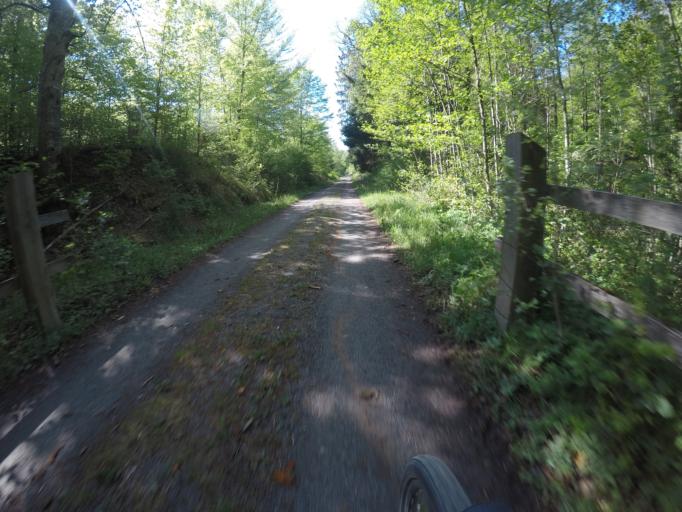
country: DE
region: Baden-Wuerttemberg
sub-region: Tuebingen Region
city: Dettenhausen
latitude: 48.5782
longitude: 9.0931
